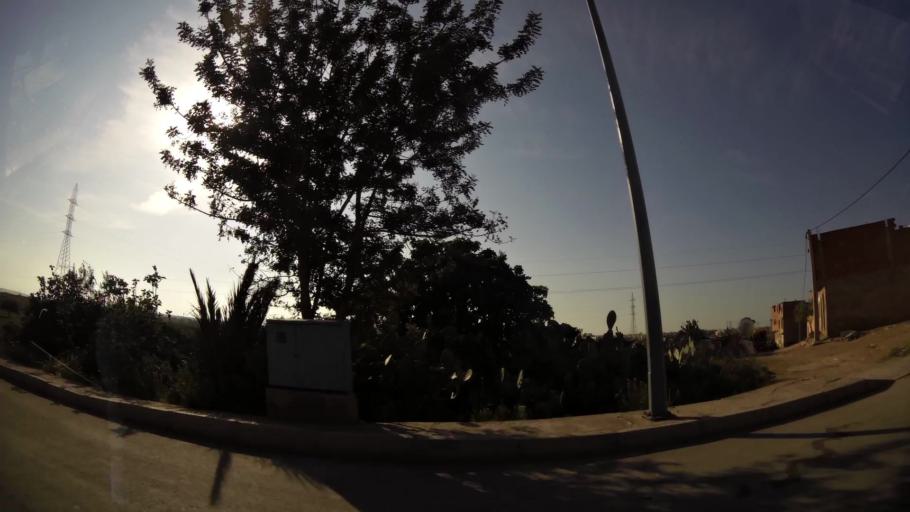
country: MA
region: Oriental
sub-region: Oujda-Angad
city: Oujda
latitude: 34.7194
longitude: -1.9054
